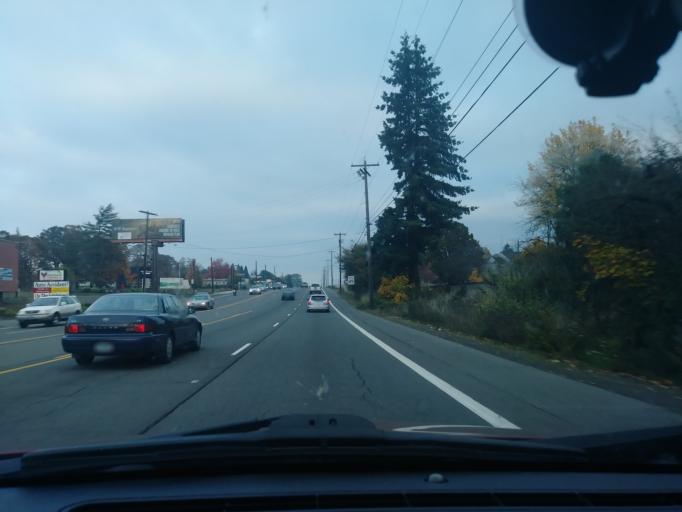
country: US
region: Oregon
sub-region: Washington County
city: Aloha
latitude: 45.4929
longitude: -122.8588
